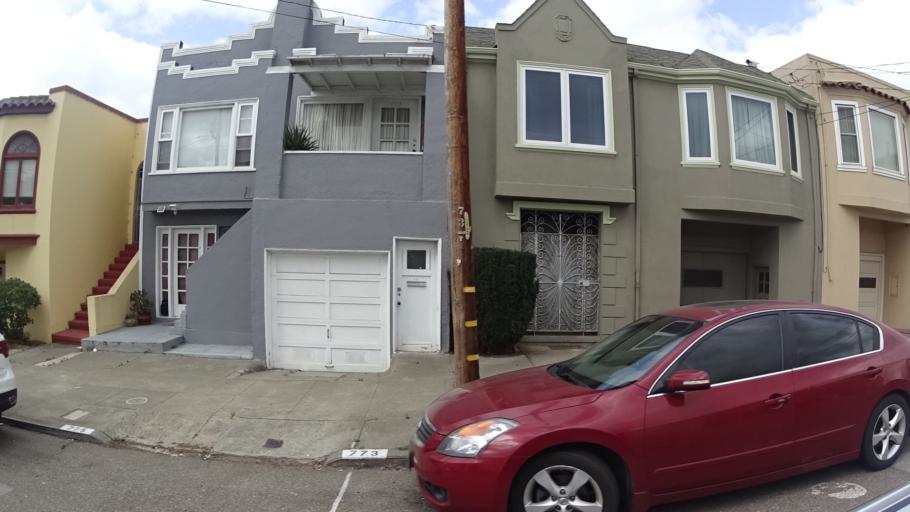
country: US
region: California
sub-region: San Mateo County
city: Daly City
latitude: 37.7741
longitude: -122.5069
